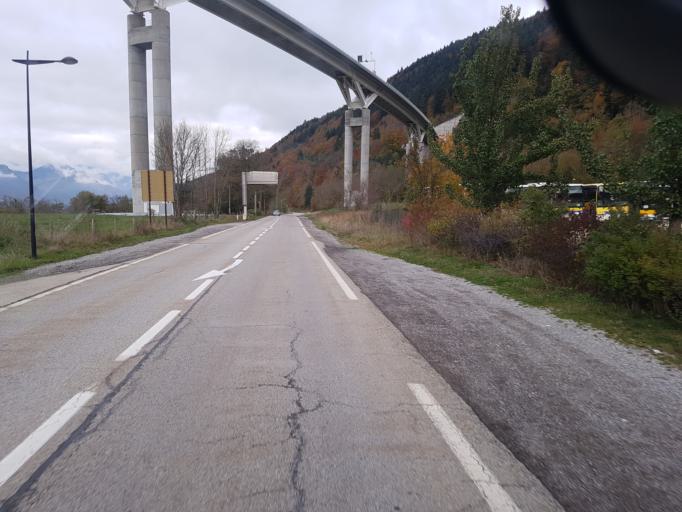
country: FR
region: Rhone-Alpes
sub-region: Departement de l'Isere
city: La Motte-Saint-Martin
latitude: 44.9308
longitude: 5.6397
